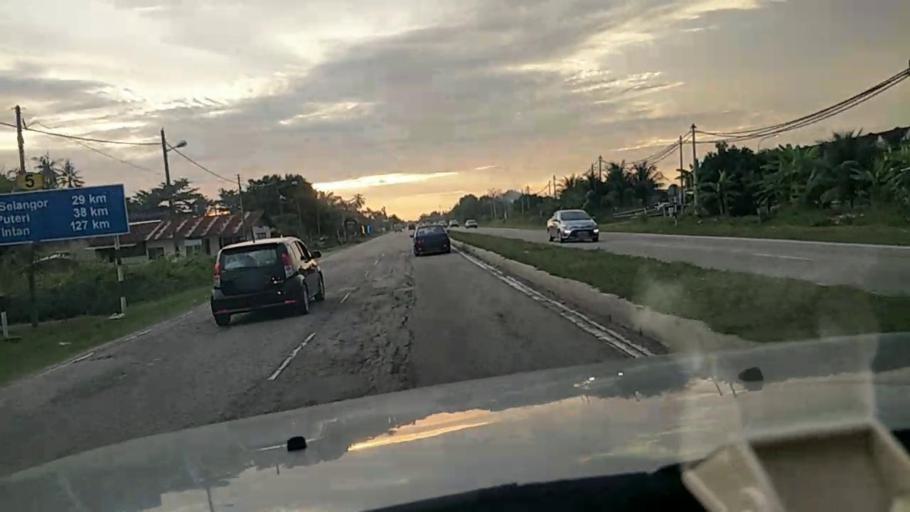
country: MY
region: Perak
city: Kampong Dungun
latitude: 3.1407
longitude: 101.3648
